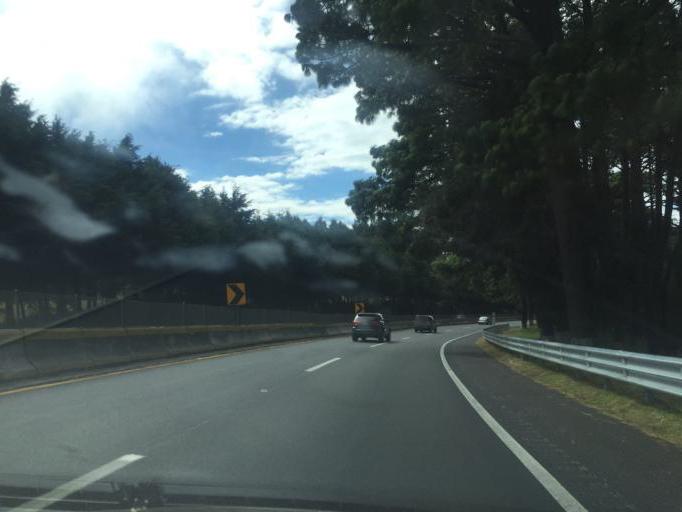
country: MX
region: Morelos
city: Tres Marias
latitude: 19.0658
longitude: -99.2379
